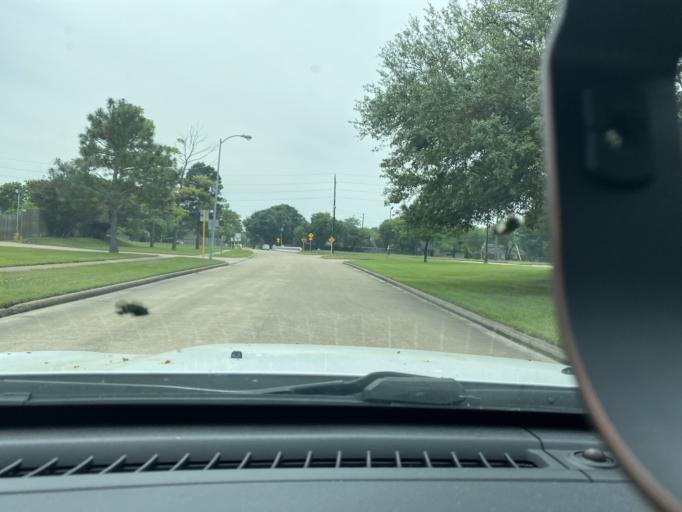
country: US
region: Texas
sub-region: Harris County
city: Jersey Village
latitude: 29.9127
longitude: -95.5735
